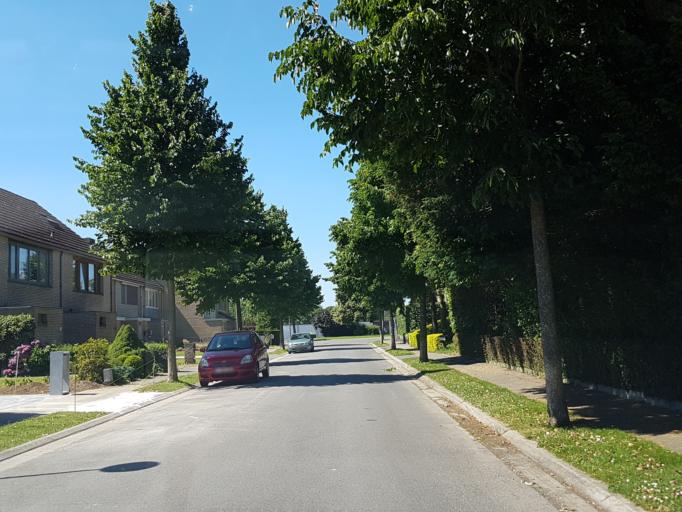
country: BE
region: Flanders
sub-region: Provincie Vlaams-Brabant
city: Dilbeek
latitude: 50.8869
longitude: 4.2573
